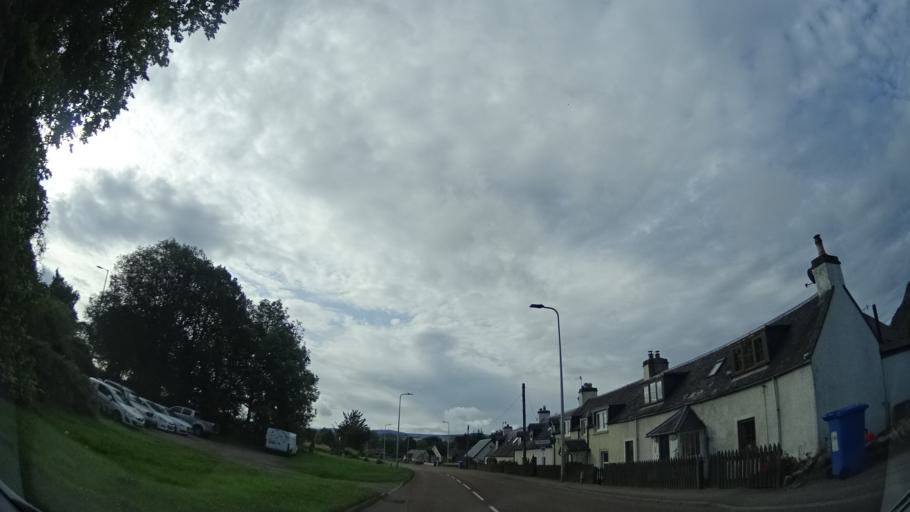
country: GB
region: Scotland
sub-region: Highland
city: Muir of Ord
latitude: 57.5662
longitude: -4.5789
